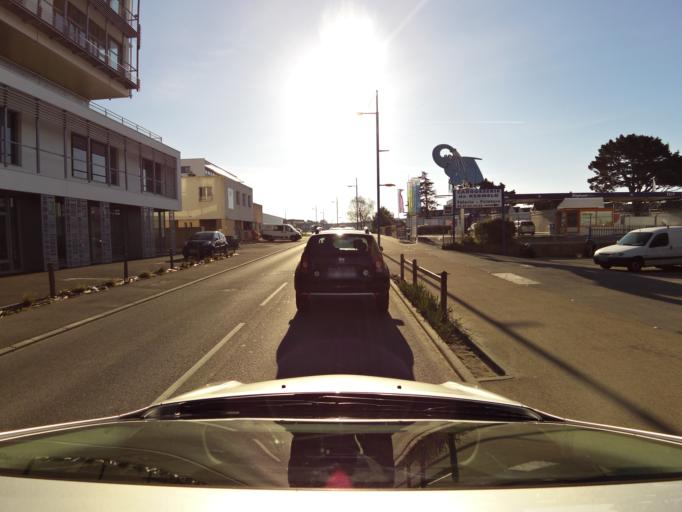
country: FR
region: Brittany
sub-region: Departement du Morbihan
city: Lorient
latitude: 47.7325
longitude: -3.3802
